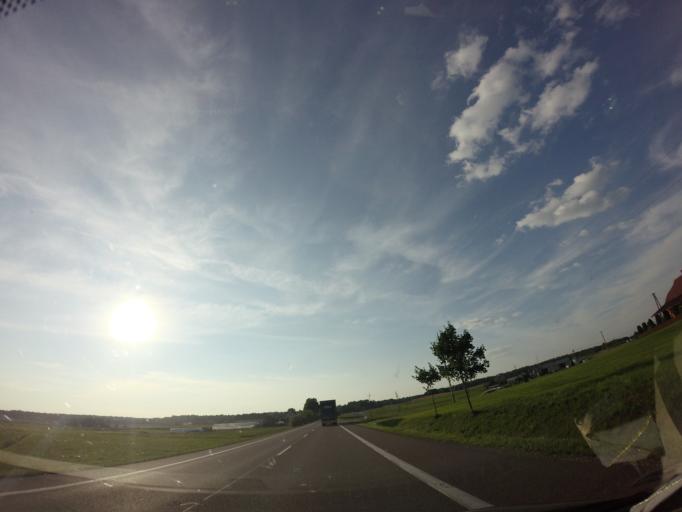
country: PL
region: Podlasie
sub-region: Powiat augustowski
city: Augustow
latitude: 53.7912
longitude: 22.9894
